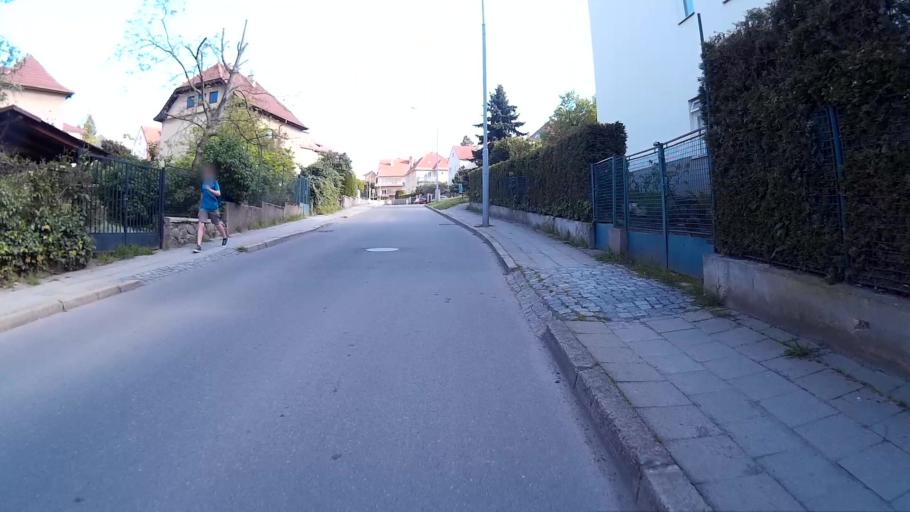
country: CZ
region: South Moravian
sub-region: Mesto Brno
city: Brno
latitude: 49.2059
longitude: 16.5804
